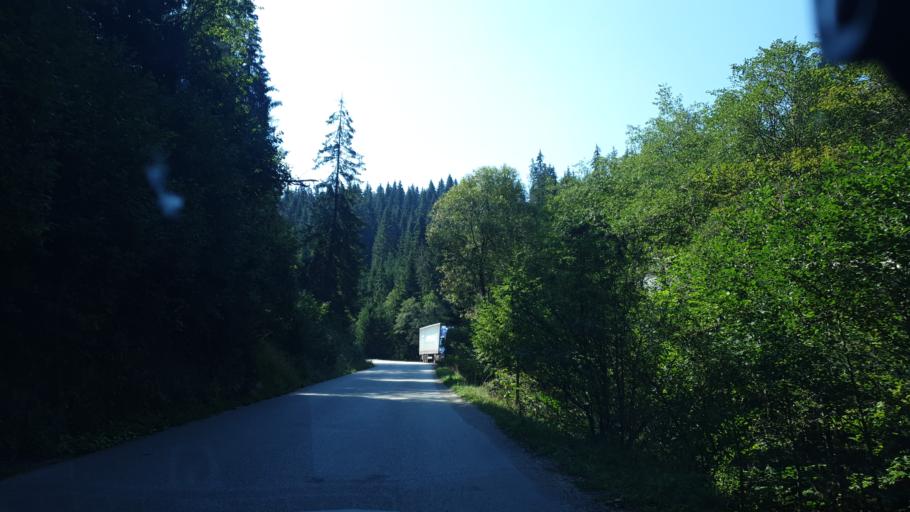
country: RS
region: Central Serbia
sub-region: Zlatiborski Okrug
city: Nova Varos
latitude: 43.4481
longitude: 19.8488
